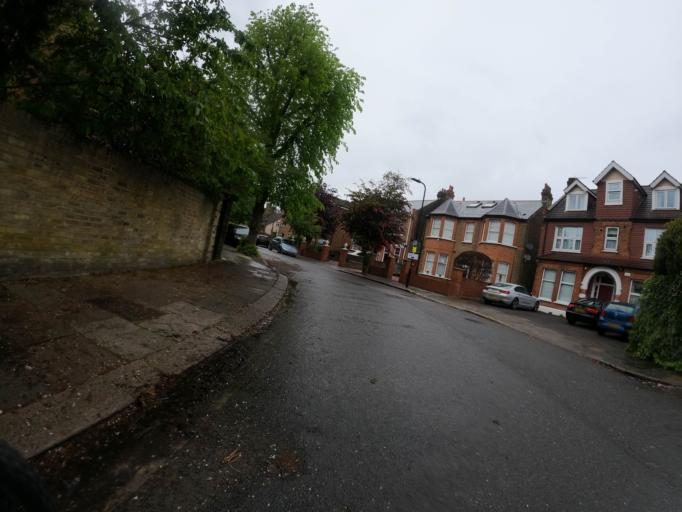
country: GB
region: England
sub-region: Greater London
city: Ealing Broadway
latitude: 51.5142
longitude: -0.2890
